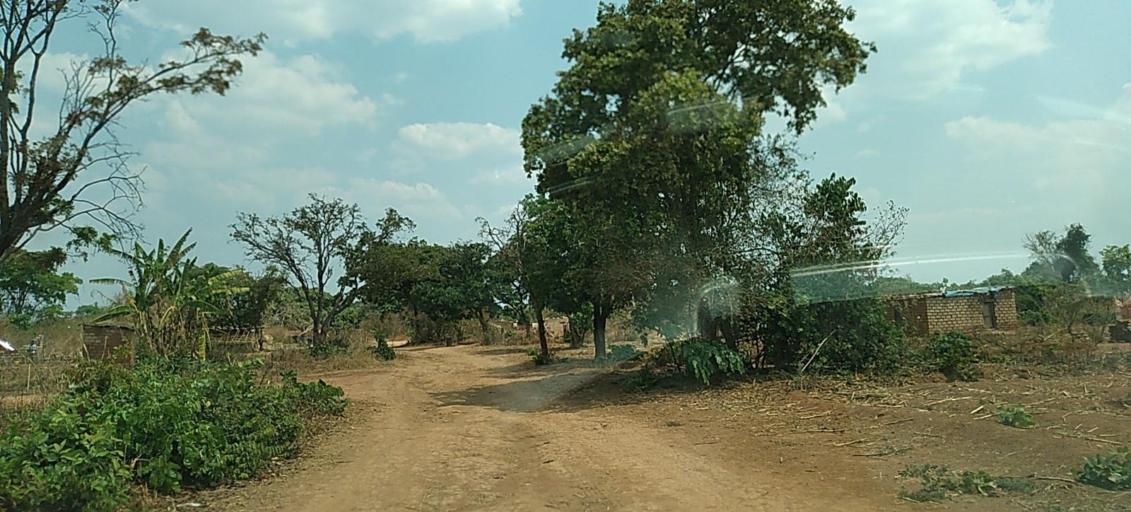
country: CD
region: Katanga
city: Kipushi
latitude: -12.0244
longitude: 27.4347
